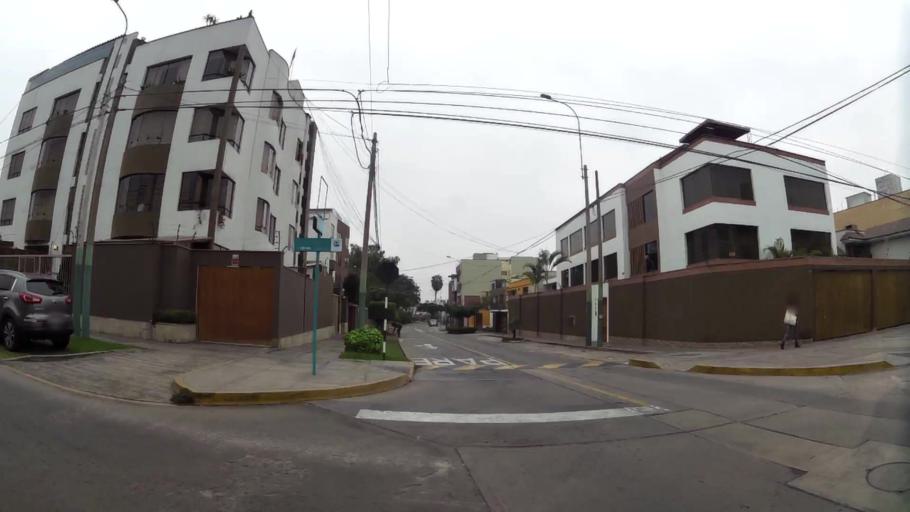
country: PE
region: Lima
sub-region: Lima
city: San Luis
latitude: -12.0896
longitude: -76.9897
